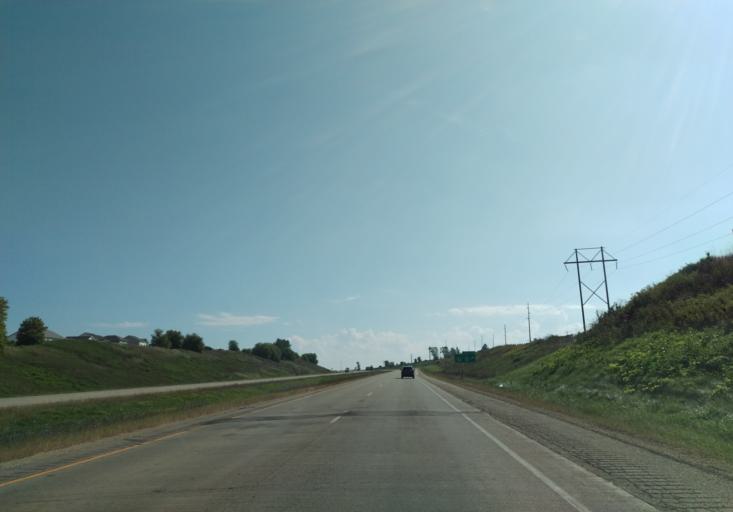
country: US
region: Wisconsin
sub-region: Dane County
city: Verona
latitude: 42.9729
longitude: -89.5237
